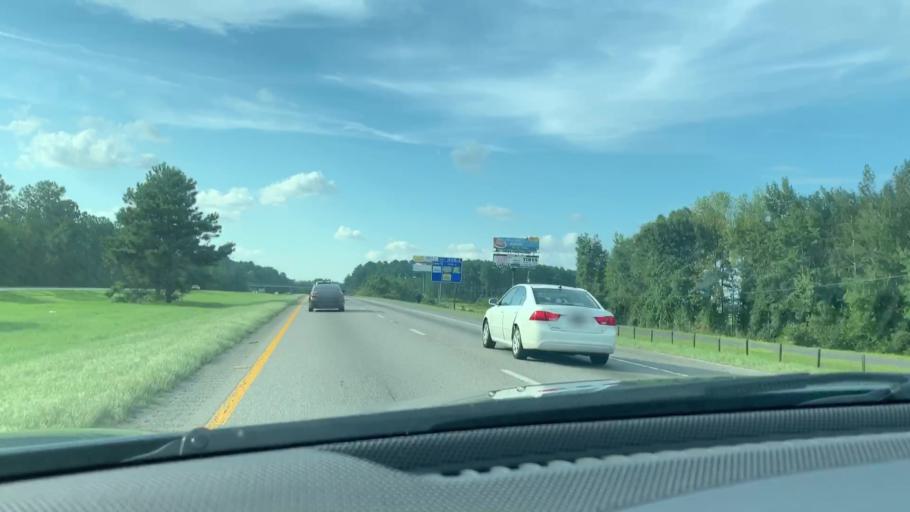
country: US
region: South Carolina
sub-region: Orangeburg County
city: Brookdale
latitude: 33.4475
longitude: -80.7167
